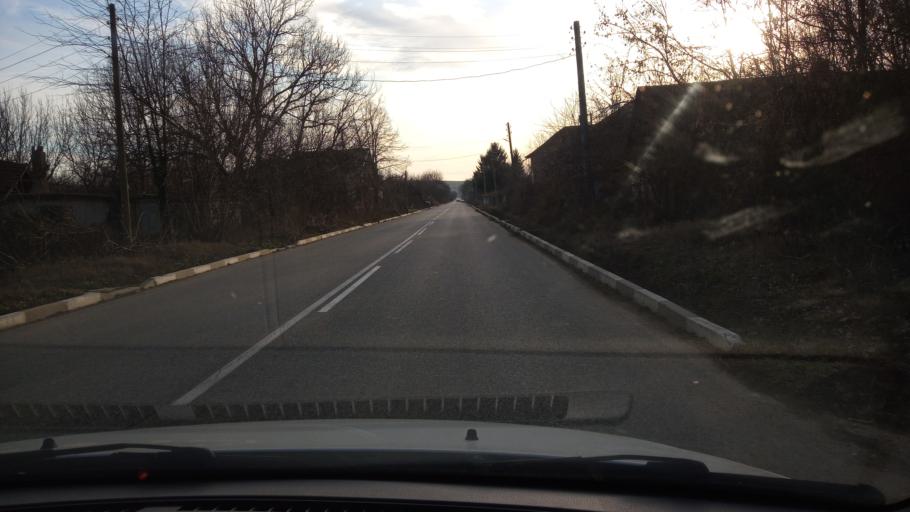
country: BG
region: Pleven
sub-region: Obshtina Pleven
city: Slavyanovo
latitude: 43.5596
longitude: 24.8683
